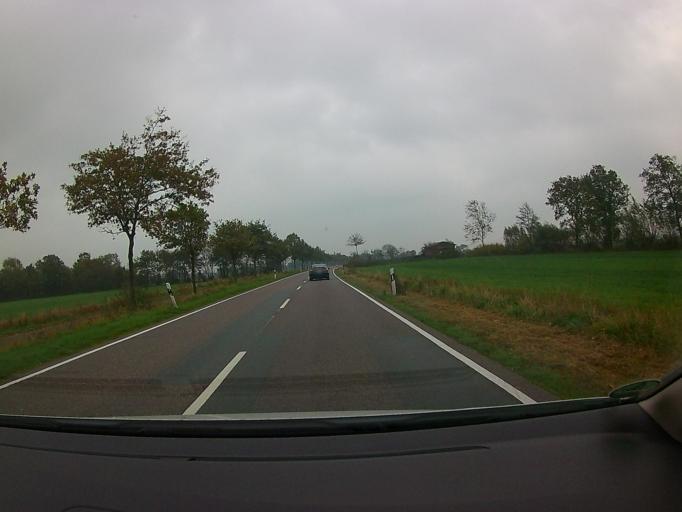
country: DE
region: Schleswig-Holstein
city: Goldelund
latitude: 54.6780
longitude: 9.1150
